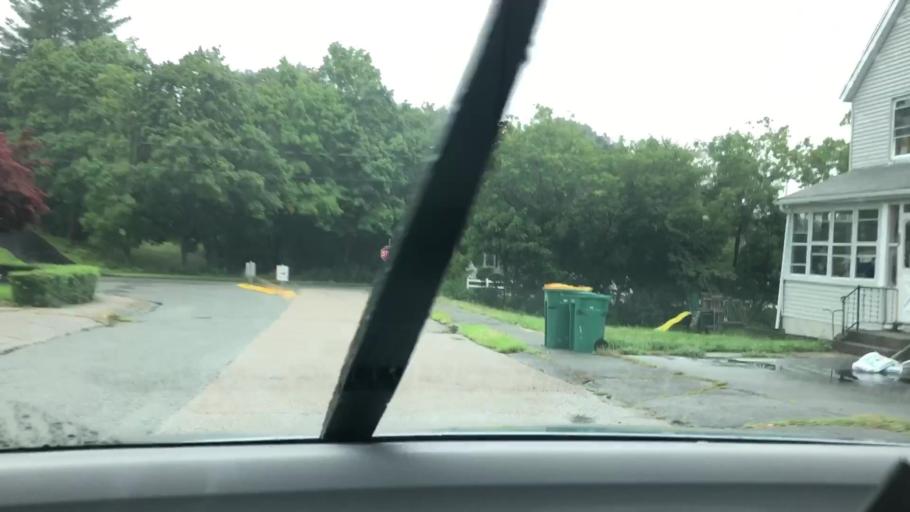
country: US
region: Massachusetts
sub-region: Norfolk County
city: Norwood
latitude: 42.2000
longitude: -71.2007
